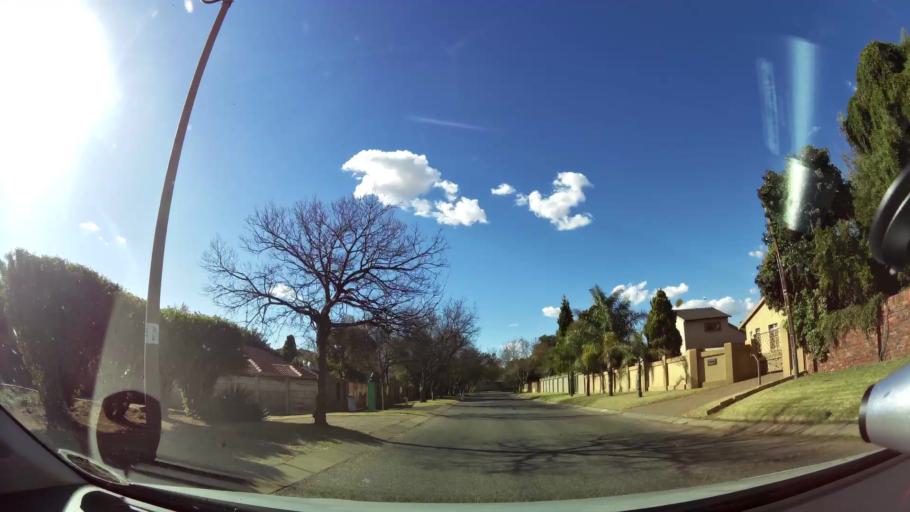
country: ZA
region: North-West
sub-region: Dr Kenneth Kaunda District Municipality
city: Klerksdorp
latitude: -26.8271
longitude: 26.6756
